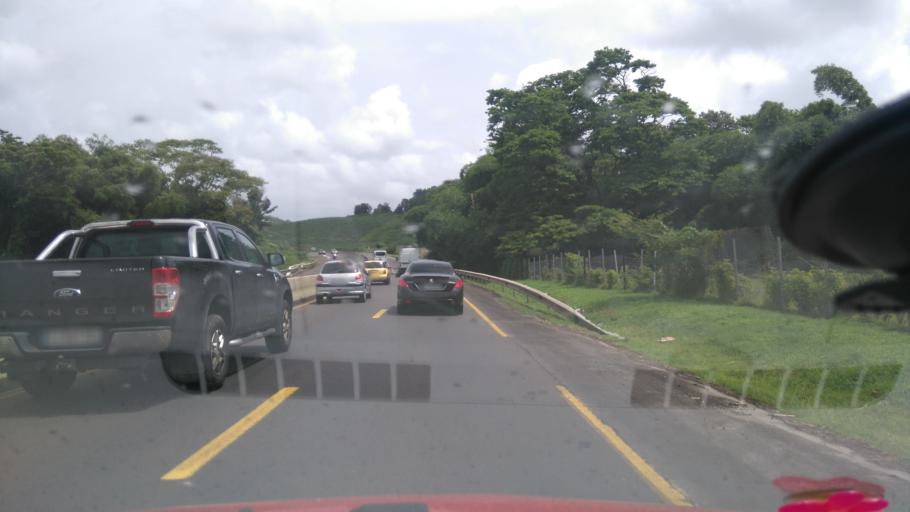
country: MQ
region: Martinique
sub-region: Martinique
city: Ducos
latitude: 14.5584
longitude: -60.9728
